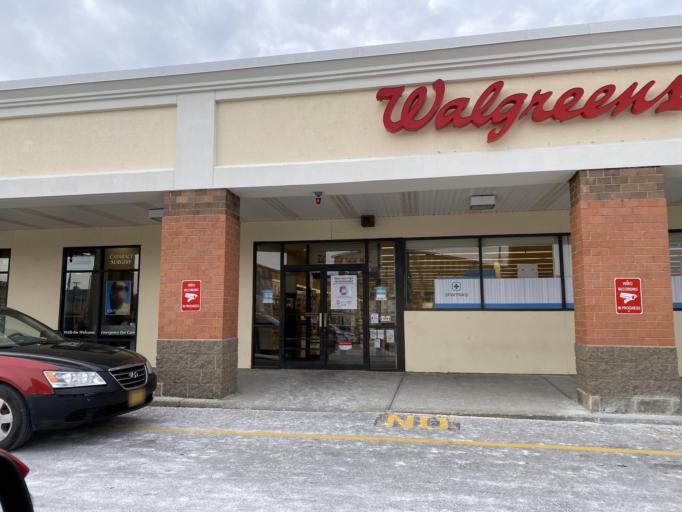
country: US
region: Massachusetts
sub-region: Bristol County
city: Fall River
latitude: 41.6951
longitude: -71.1406
